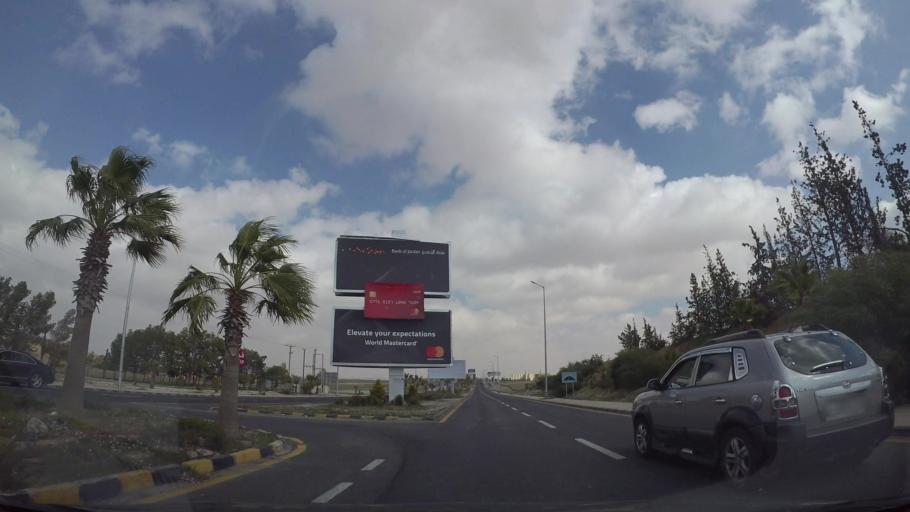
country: JO
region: Amman
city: Al Jizah
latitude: 31.7224
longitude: 35.9539
